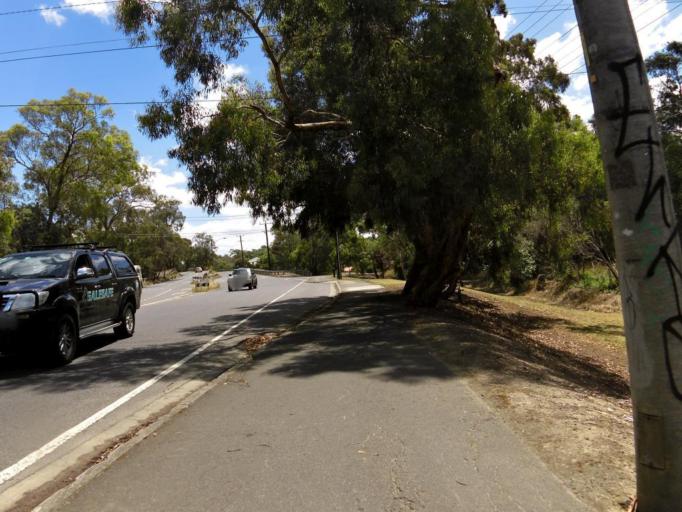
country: AU
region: Victoria
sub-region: Nillumbik
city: Eltham North
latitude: -37.7042
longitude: 145.1569
